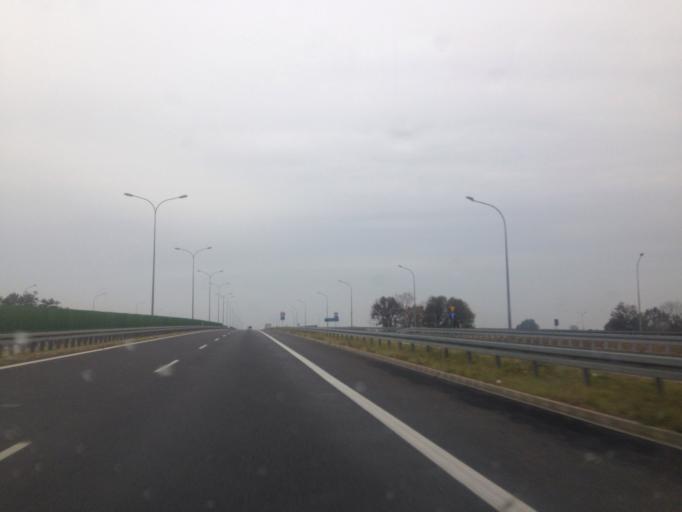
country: PL
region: Greater Poland Voivodeship
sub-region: Powiat poznanski
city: Kostrzyn
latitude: 52.3987
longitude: 17.2581
